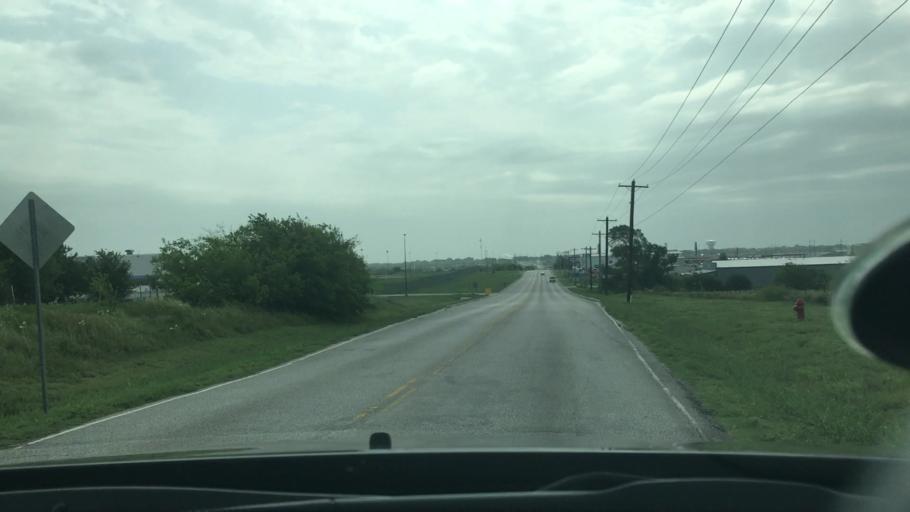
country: US
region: Oklahoma
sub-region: Carter County
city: Ardmore
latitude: 34.2020
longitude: -97.1756
